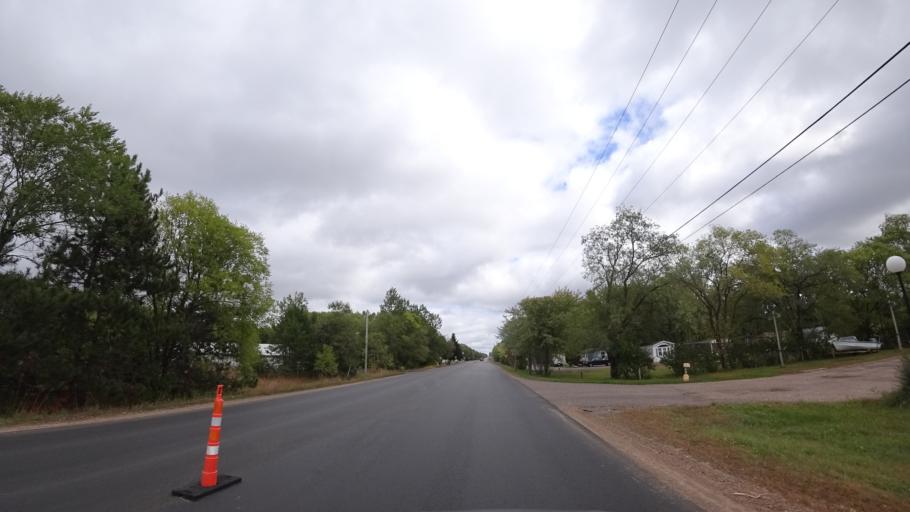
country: US
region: Wisconsin
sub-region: Chippewa County
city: Lake Wissota
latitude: 44.9296
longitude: -91.2711
